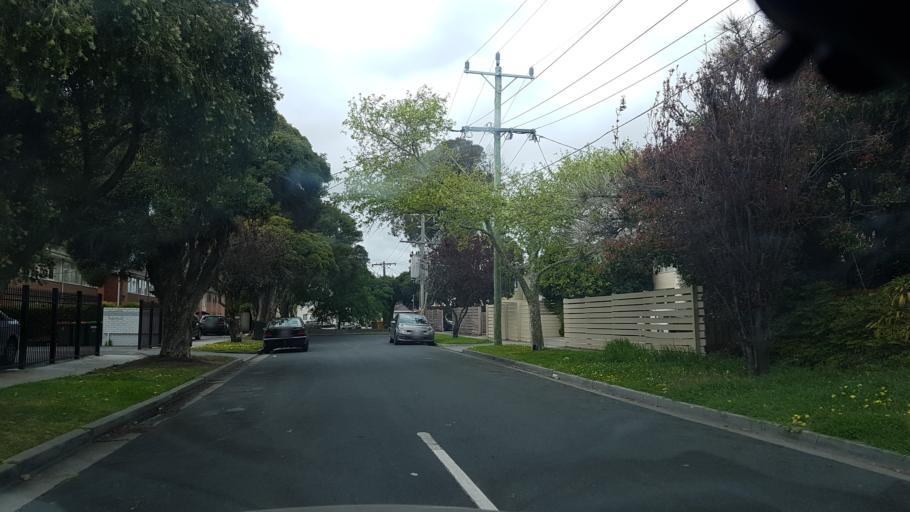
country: AU
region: Victoria
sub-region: Bayside
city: Moorabbin
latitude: -37.9332
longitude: 145.0440
